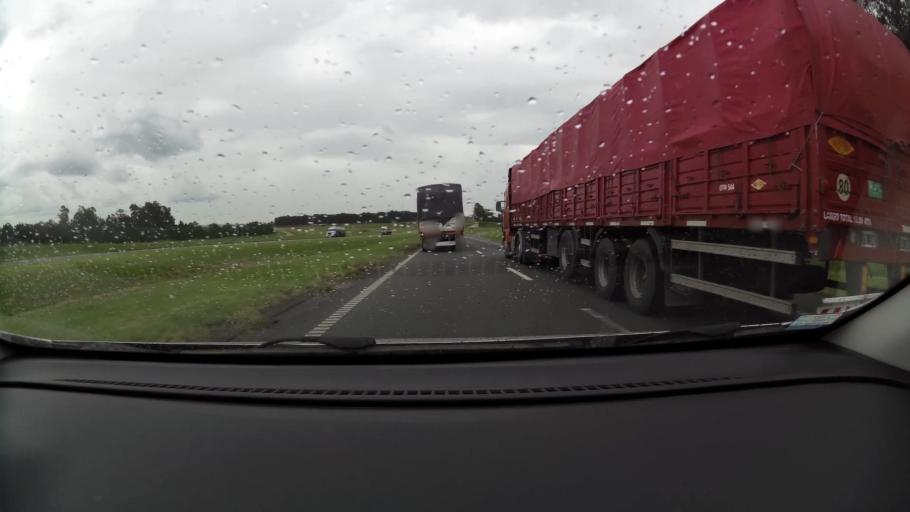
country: AR
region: Buenos Aires
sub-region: Partido de Baradero
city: Baradero
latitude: -33.8441
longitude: -59.5589
